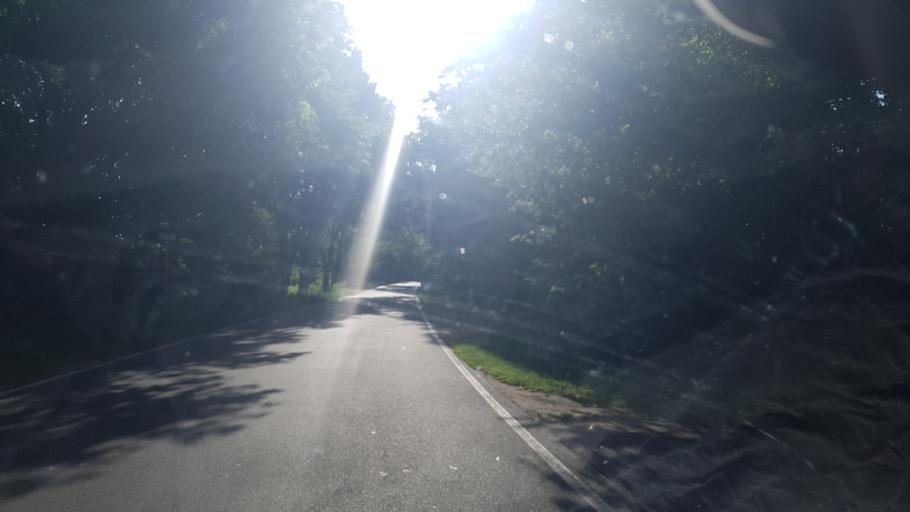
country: DE
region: Brandenburg
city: Luckau
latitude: 51.8259
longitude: 13.7304
